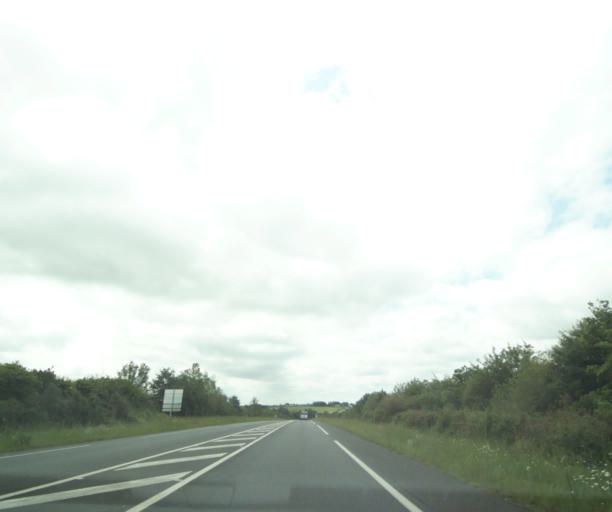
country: FR
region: Poitou-Charentes
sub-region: Departement des Deux-Sevres
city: Viennay
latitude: 46.7604
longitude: -0.2216
